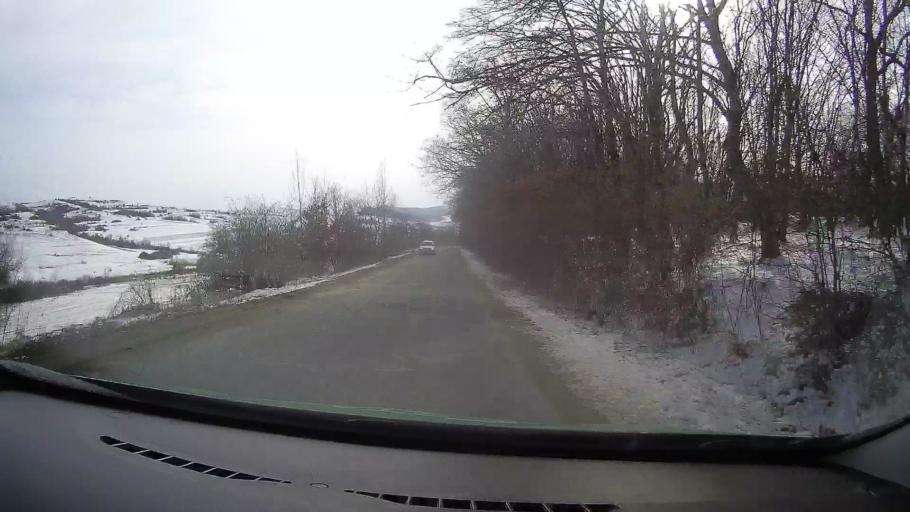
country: RO
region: Sibiu
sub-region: Comuna Bradeni
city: Bradeni
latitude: 46.1007
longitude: 24.8377
